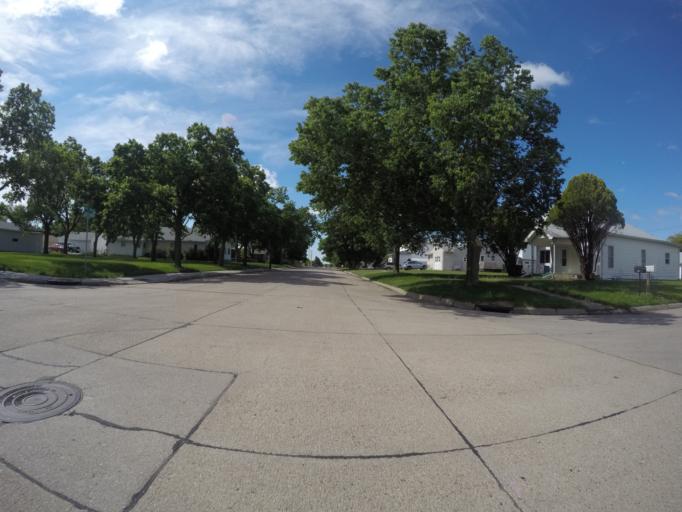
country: US
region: Nebraska
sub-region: Buffalo County
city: Kearney
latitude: 40.6873
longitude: -99.0875
